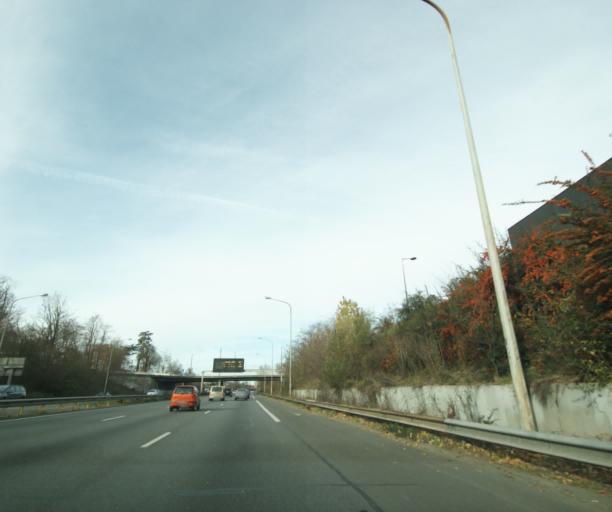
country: FR
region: Midi-Pyrenees
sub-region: Departement de la Haute-Garonne
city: Blagnac
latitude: 43.5906
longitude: 1.3995
